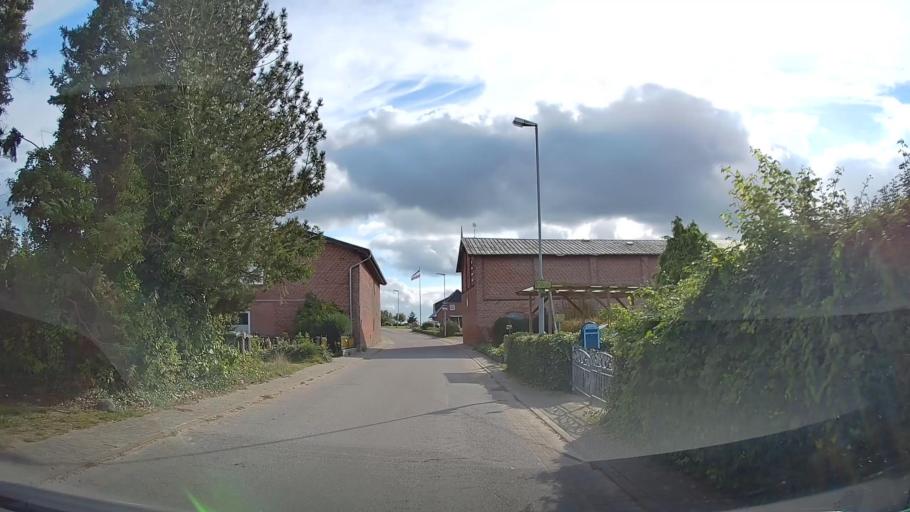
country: DE
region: Schleswig-Holstein
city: Steinberg
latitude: 54.7993
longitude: 9.7558
